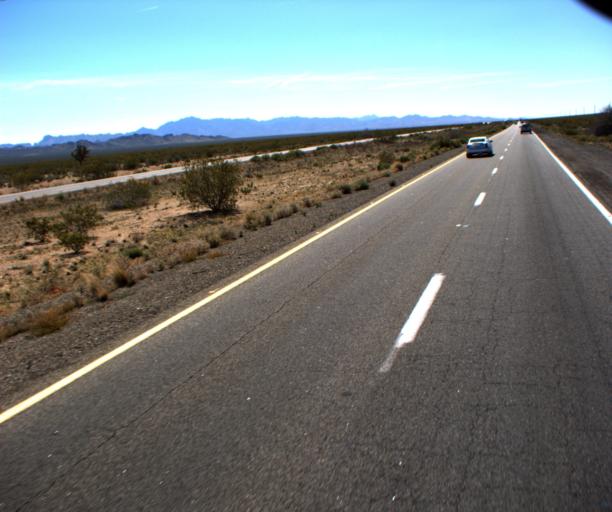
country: US
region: Arizona
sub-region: Mohave County
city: Dolan Springs
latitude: 35.6532
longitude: -114.4439
